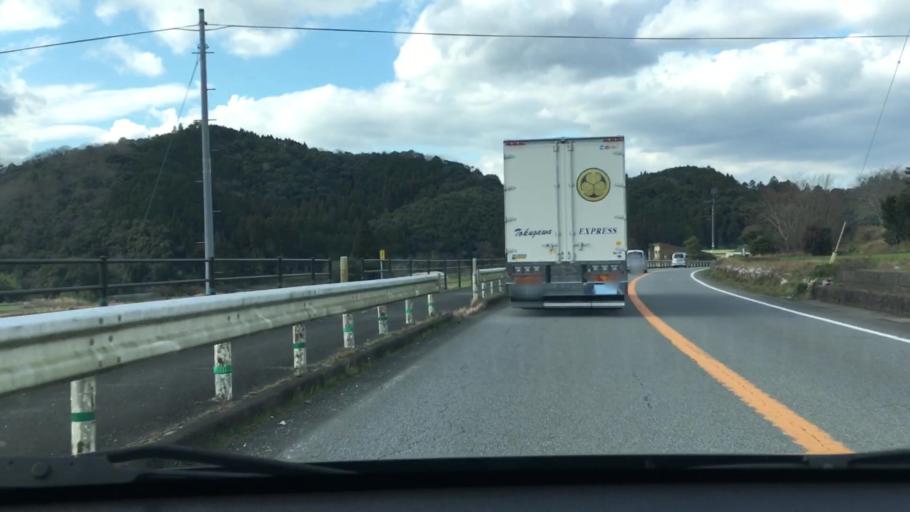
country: JP
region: Oita
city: Usuki
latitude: 33.0114
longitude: 131.7021
